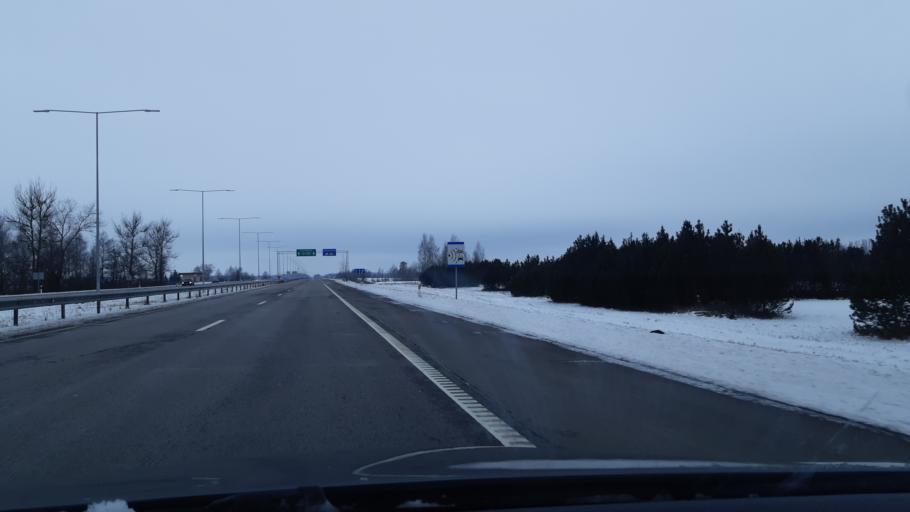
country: LT
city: Vilkija
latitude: 55.1354
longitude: 23.7305
